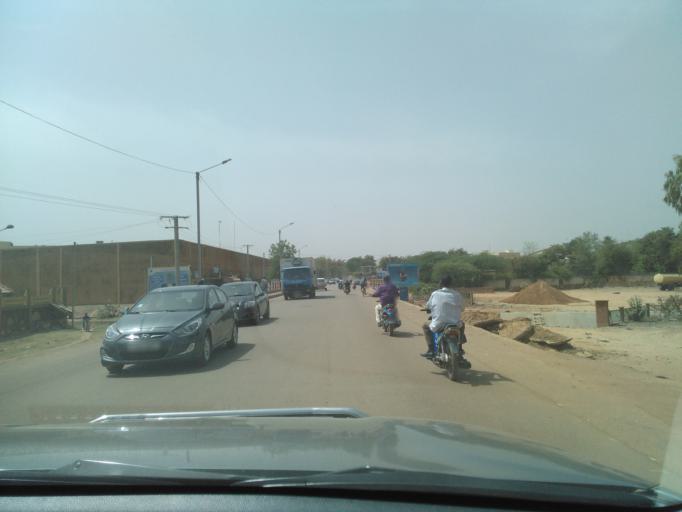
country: BF
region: Centre
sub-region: Kadiogo Province
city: Ouagadougou
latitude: 12.3556
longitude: -1.5367
